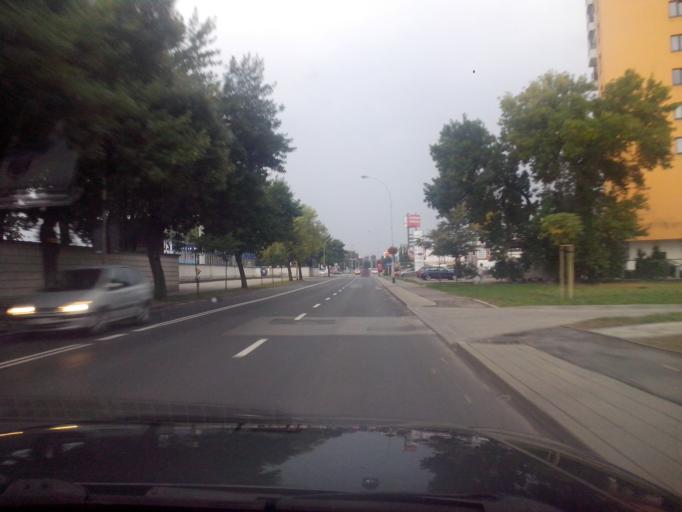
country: PL
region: Subcarpathian Voivodeship
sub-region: Rzeszow
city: Rzeszow
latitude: 50.0224
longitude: 21.9948
